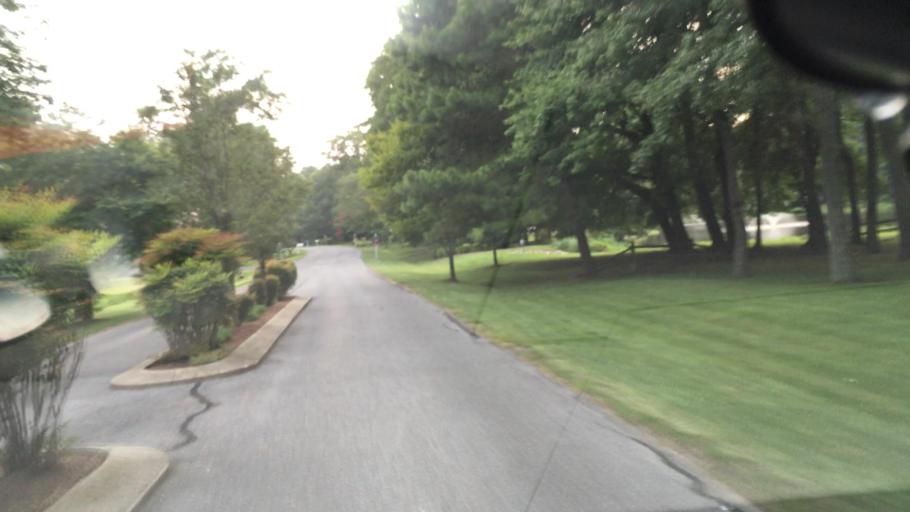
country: US
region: Delaware
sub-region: Sussex County
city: Rehoboth Beach
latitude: 38.6999
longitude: -75.0835
